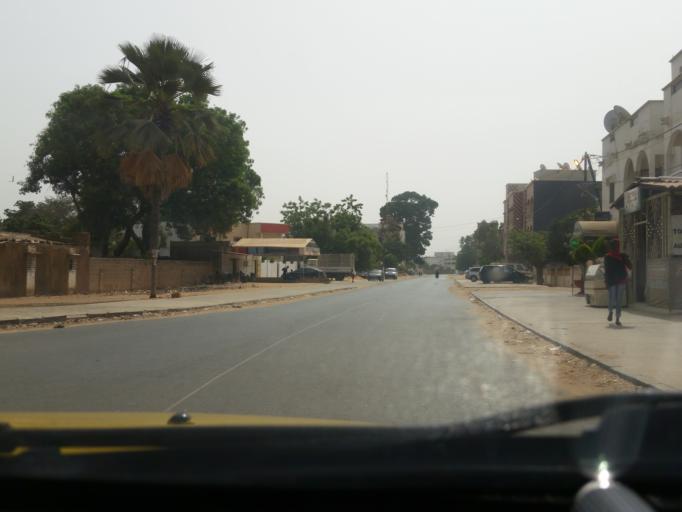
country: SN
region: Thies
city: Thies Nones
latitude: 14.7894
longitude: -16.9347
